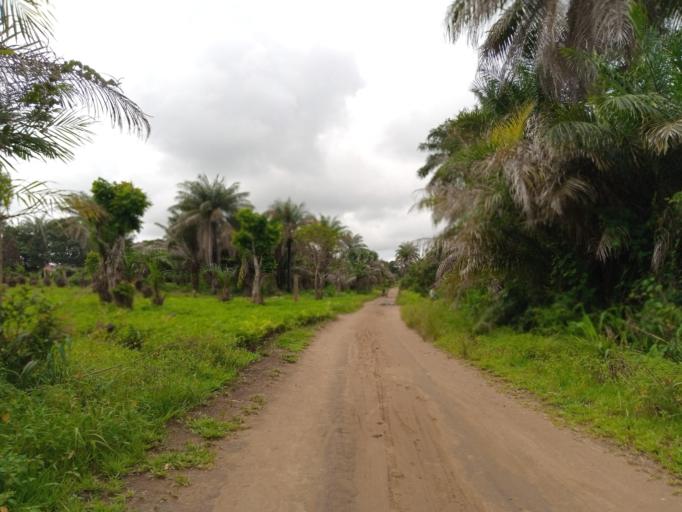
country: SL
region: Northern Province
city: Masoyila
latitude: 8.5828
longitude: -13.1916
